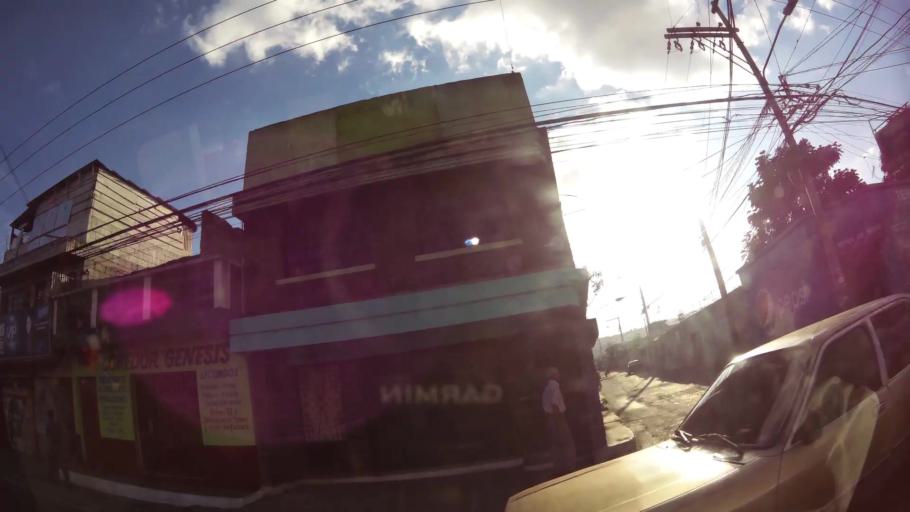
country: GT
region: Guatemala
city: Villa Nueva
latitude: 14.5200
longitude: -90.5827
